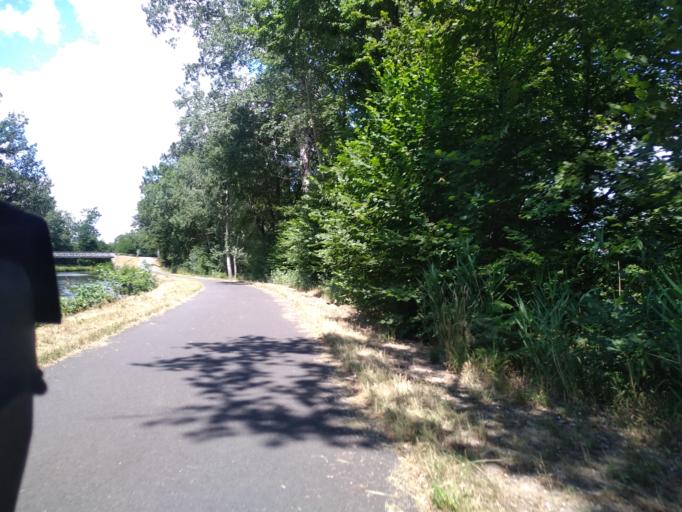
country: FR
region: Rhone-Alpes
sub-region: Departement de la Loire
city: Briennon
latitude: 46.1186
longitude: 4.0778
